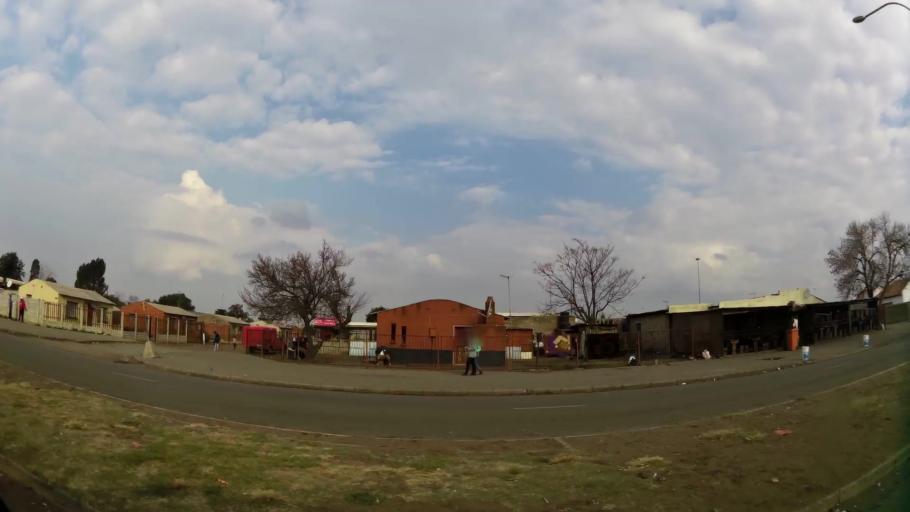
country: ZA
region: Gauteng
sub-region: Sedibeng District Municipality
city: Vanderbijlpark
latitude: -26.6835
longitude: 27.8771
